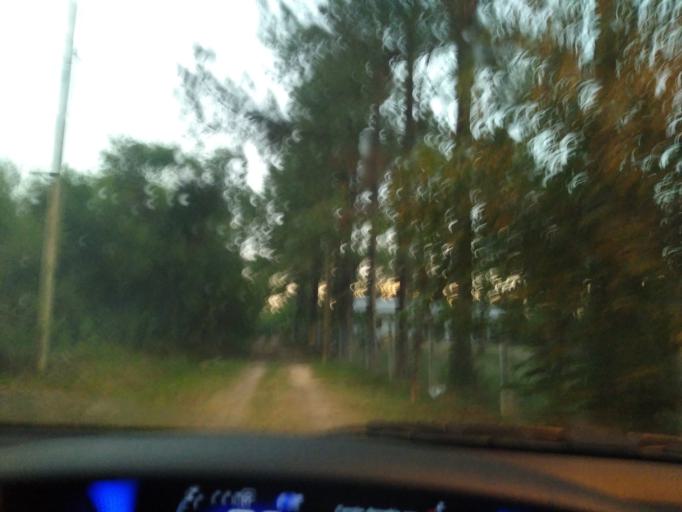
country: AR
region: Chaco
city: Puerto Tirol
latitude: -27.3763
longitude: -59.0846
